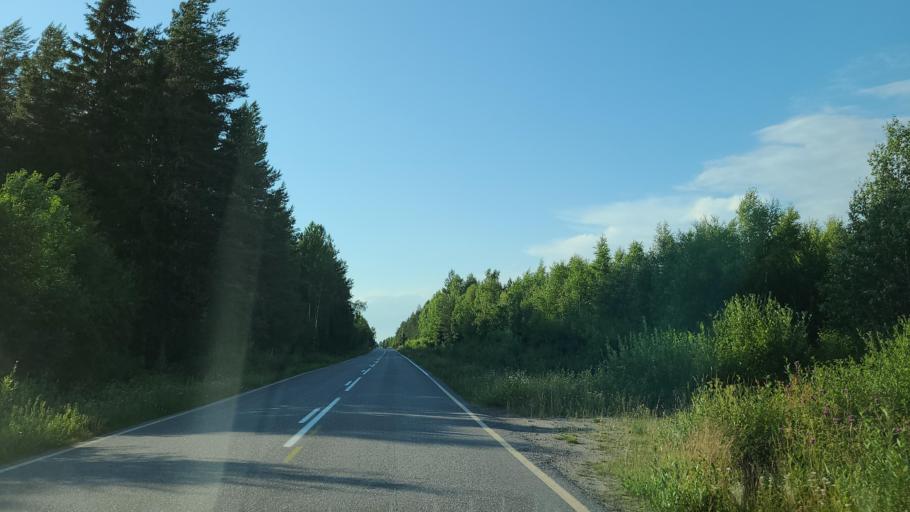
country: FI
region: Ostrobothnia
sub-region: Vaasa
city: Replot
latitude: 63.2470
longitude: 21.3782
